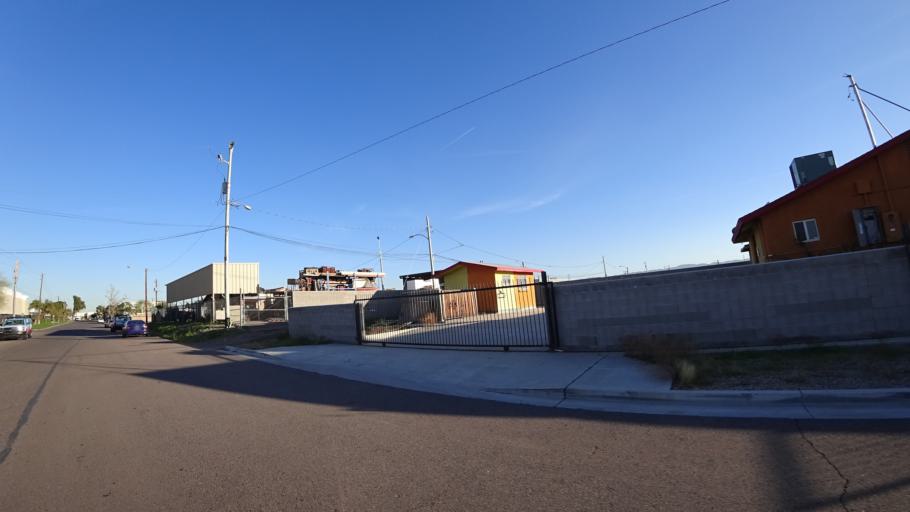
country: US
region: Arizona
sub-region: Maricopa County
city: Phoenix
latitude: 33.4258
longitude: -112.0432
